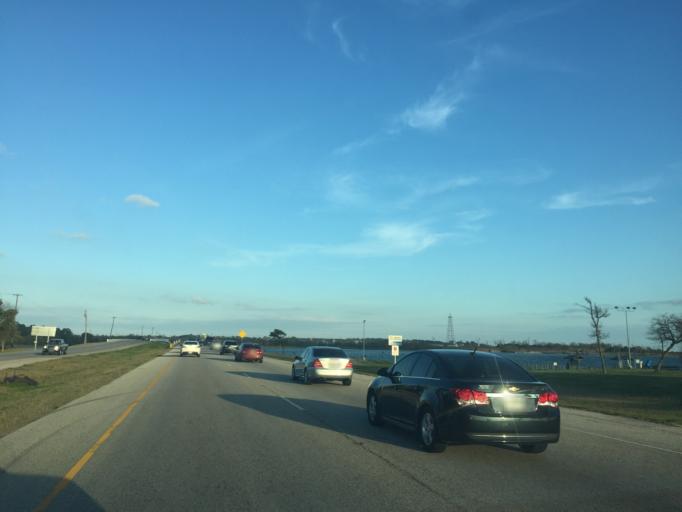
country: US
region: Texas
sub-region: Harris County
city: Baytown
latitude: 29.7137
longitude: -94.9943
